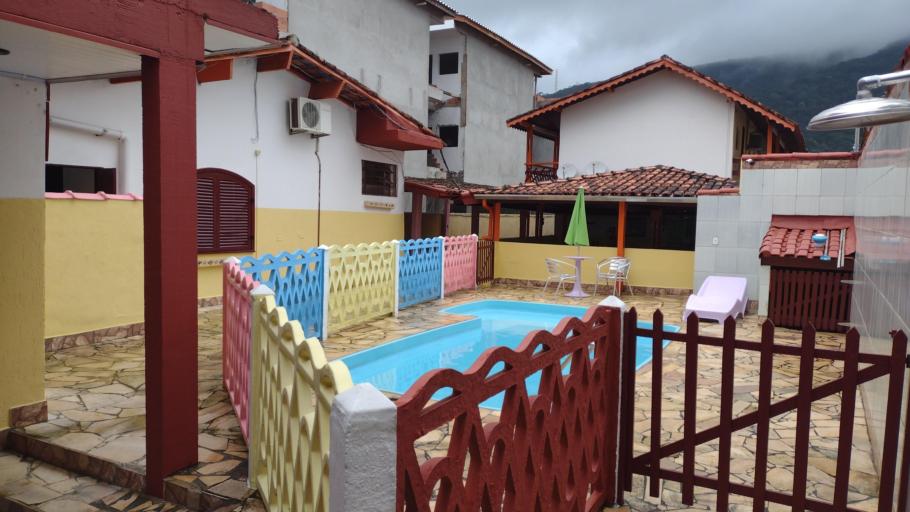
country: BR
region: Sao Paulo
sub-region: Ubatuba
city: Ubatuba
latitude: -23.5430
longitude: -45.2314
